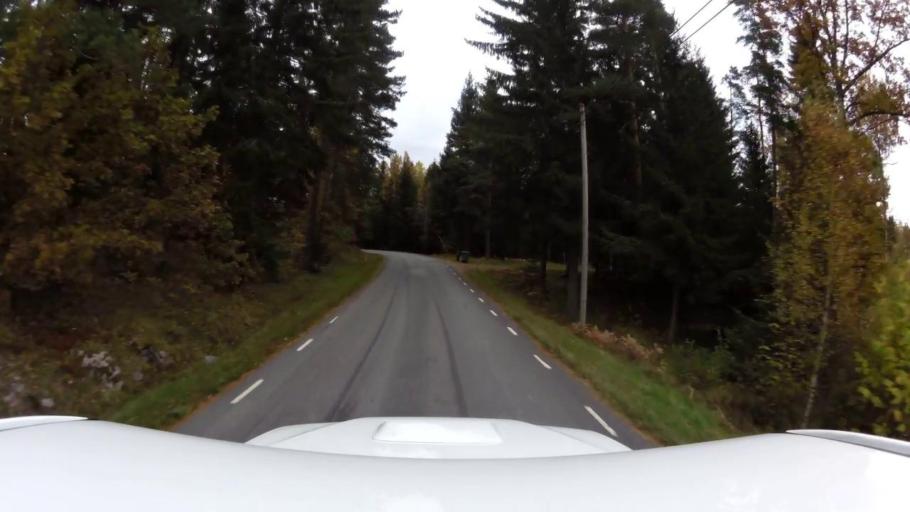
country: SE
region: OEstergoetland
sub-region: Linkopings Kommun
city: Ljungsbro
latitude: 58.5437
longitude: 15.4151
